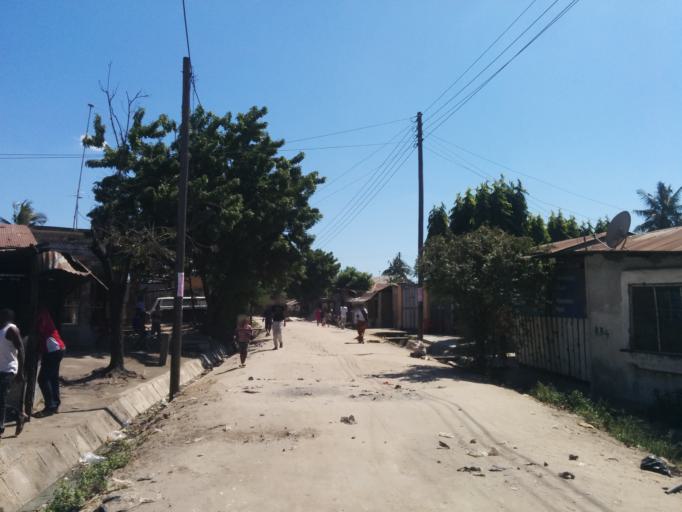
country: TZ
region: Dar es Salaam
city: Magomeni
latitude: -6.7922
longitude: 39.2353
